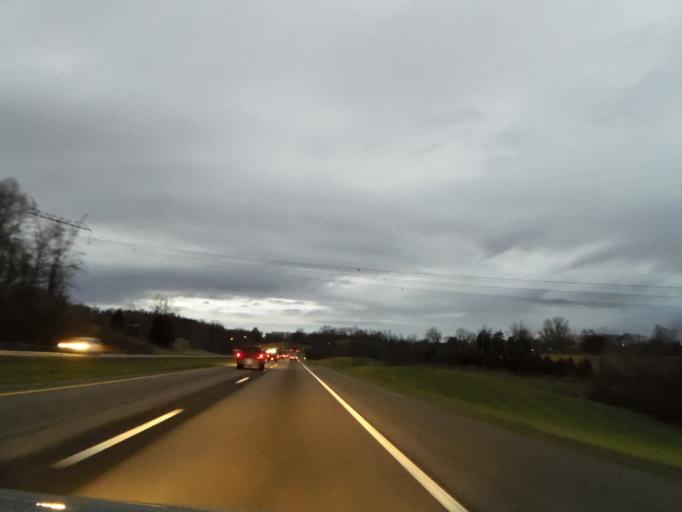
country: US
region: Tennessee
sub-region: Washington County
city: Oak Grove
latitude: 36.3907
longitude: -82.4439
